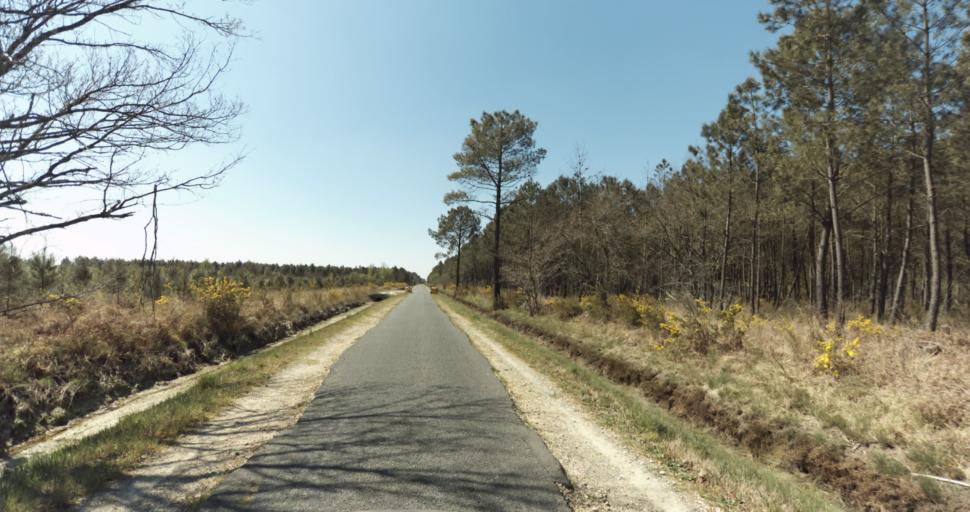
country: FR
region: Aquitaine
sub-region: Departement de la Gironde
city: Saint-Aubin-de-Medoc
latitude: 44.7889
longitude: -0.7613
